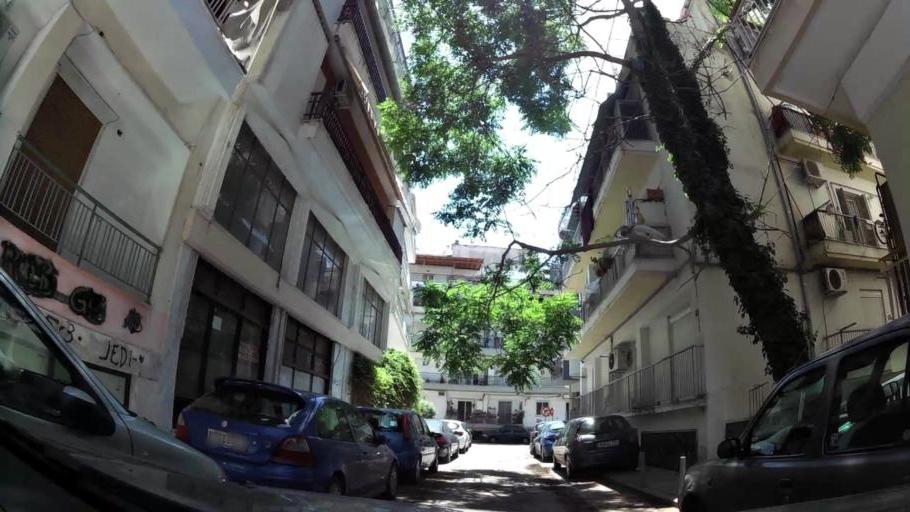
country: GR
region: Central Macedonia
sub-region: Nomos Thessalonikis
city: Triandria
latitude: 40.6057
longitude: 22.9547
